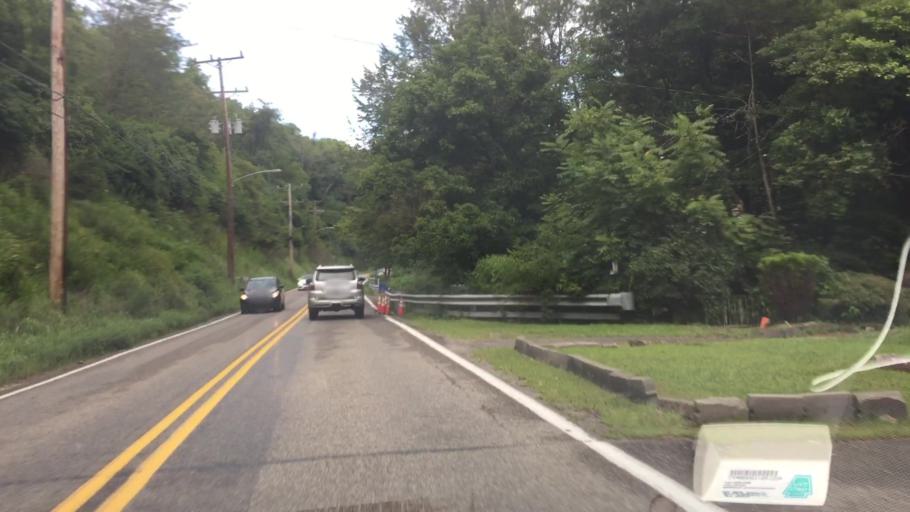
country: US
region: Pennsylvania
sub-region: Allegheny County
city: Heidelberg
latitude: 40.3806
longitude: -80.0846
